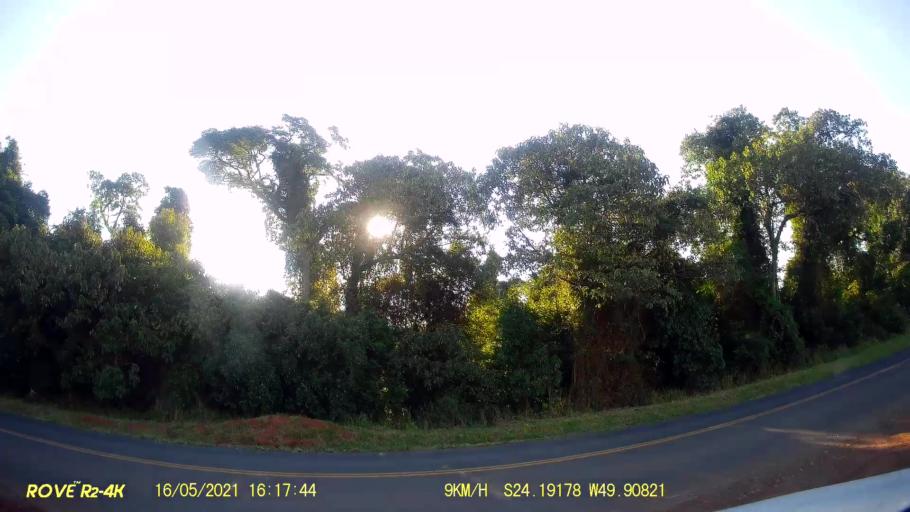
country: BR
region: Parana
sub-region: Jaguariaiva
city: Jaguariaiva
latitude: -24.1918
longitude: -49.9082
